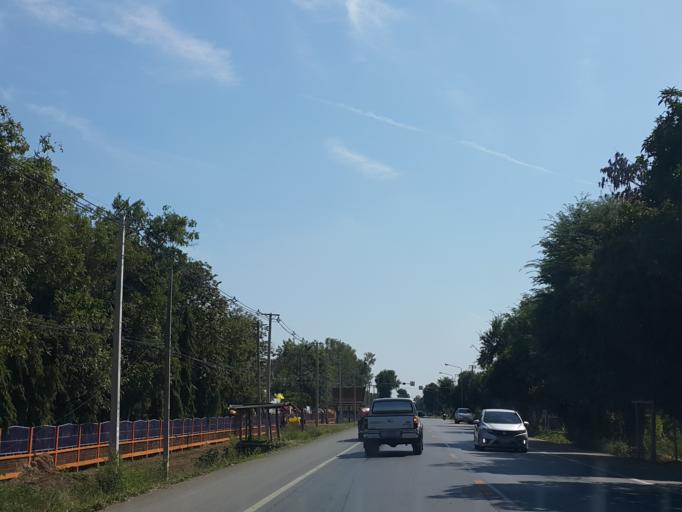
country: TH
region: Sukhothai
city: Sawankhalok
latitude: 17.2614
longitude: 99.8465
